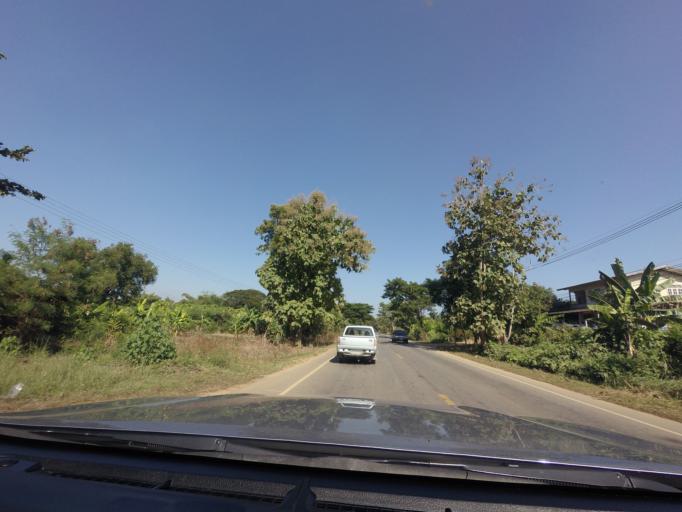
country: TH
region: Sukhothai
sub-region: Amphoe Si Satchanalai
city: Si Satchanalai
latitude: 17.6745
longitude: 99.6970
